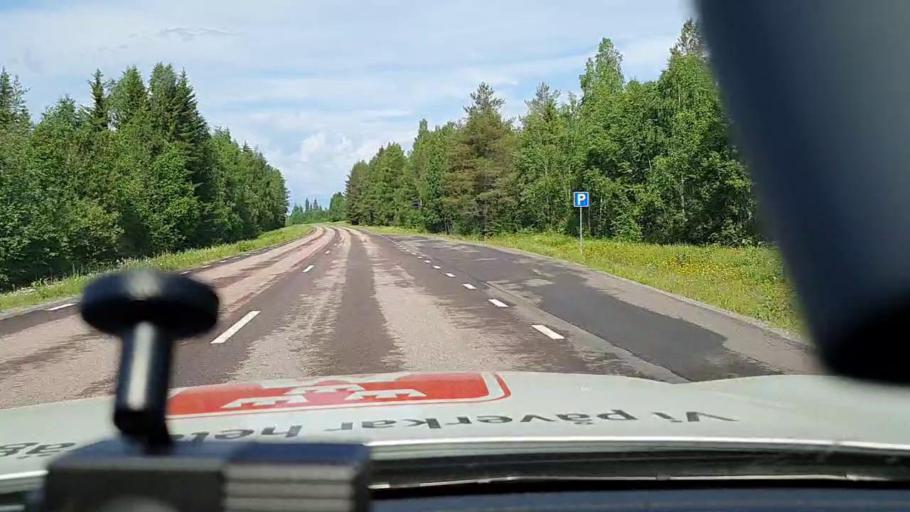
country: SE
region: Norrbotten
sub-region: Alvsbyns Kommun
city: AElvsbyn
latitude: 66.0216
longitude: 21.1327
